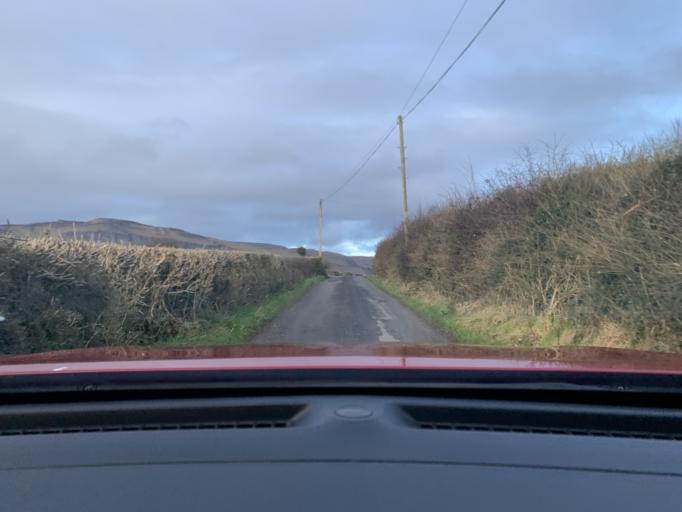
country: IE
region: Connaught
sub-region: Sligo
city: Sligo
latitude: 54.3123
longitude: -8.4521
